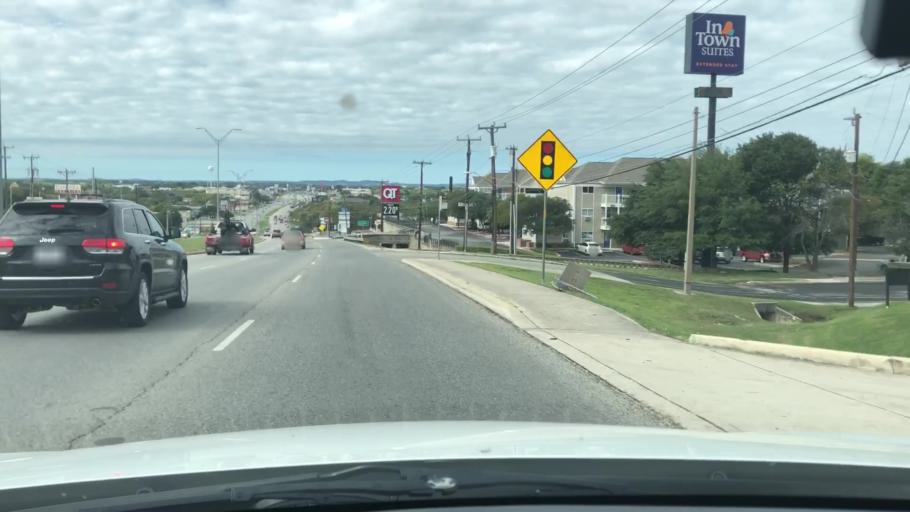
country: US
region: Texas
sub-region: Bexar County
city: Leon Valley
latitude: 29.4895
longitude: -98.6103
